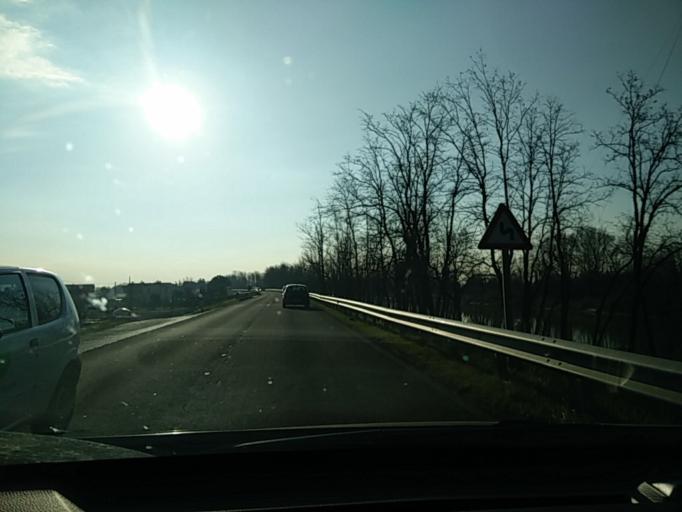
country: IT
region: Veneto
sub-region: Provincia di Venezia
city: Eraclea
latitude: 45.5811
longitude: 12.6552
